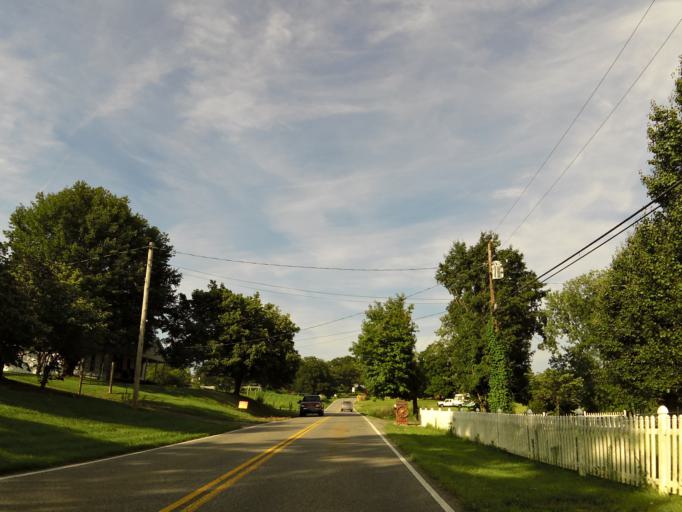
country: US
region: Tennessee
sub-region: Sevier County
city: Seymour
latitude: 35.8525
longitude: -83.7811
